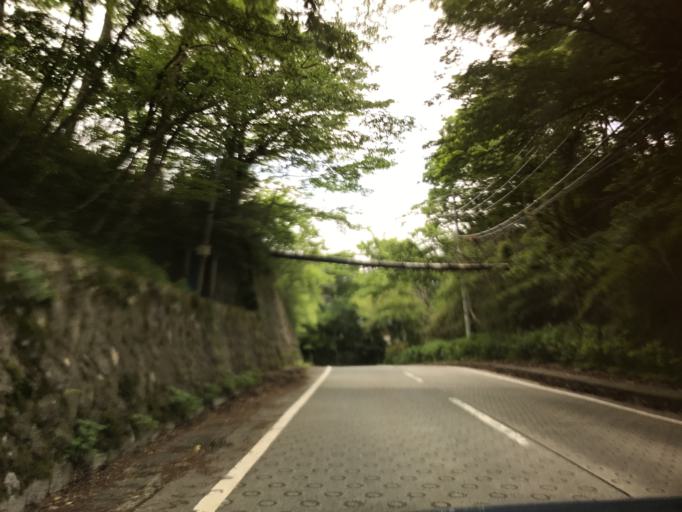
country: JP
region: Kanagawa
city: Hakone
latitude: 35.2568
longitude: 139.0198
